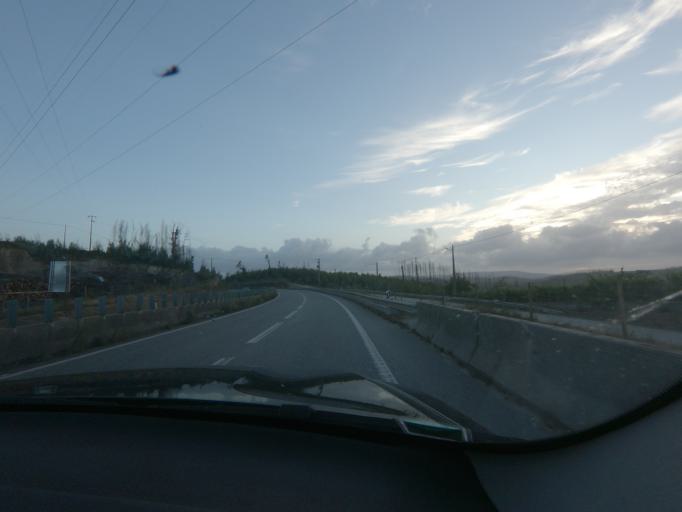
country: PT
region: Viseu
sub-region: Mortagua
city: Mortagua
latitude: 40.3537
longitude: -8.2004
